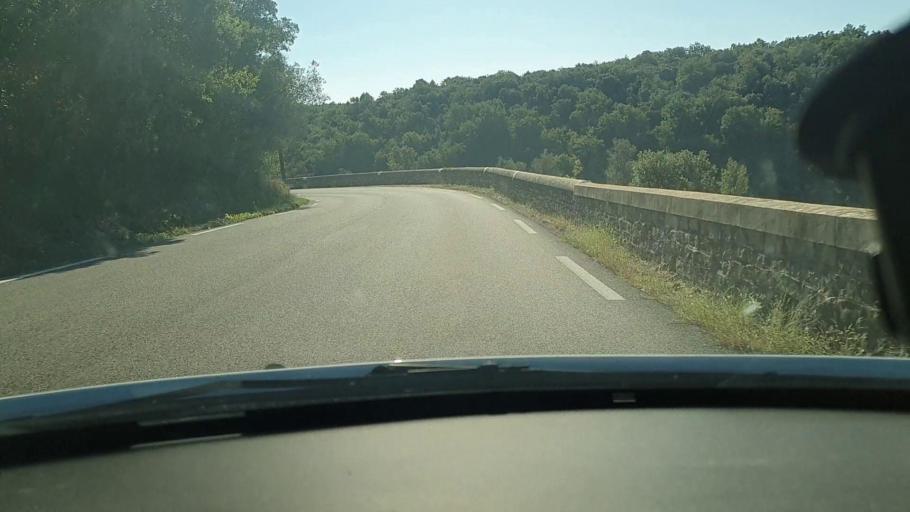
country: FR
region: Languedoc-Roussillon
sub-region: Departement du Gard
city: Goudargues
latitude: 44.2930
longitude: 4.4836
